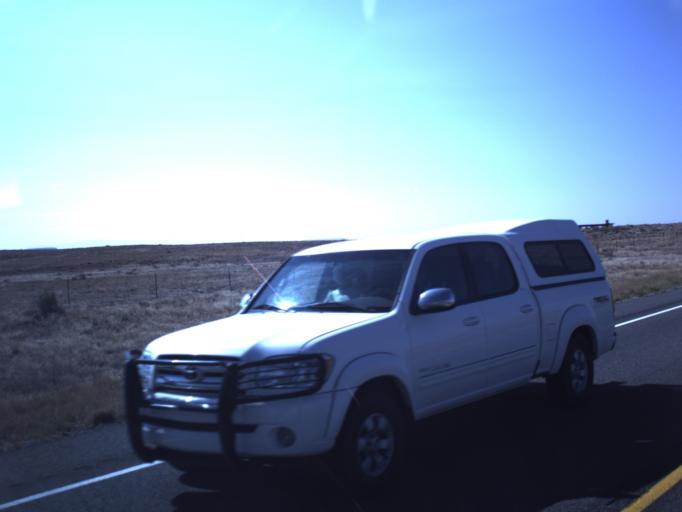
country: US
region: Utah
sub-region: San Juan County
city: Blanding
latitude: 37.4014
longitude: -109.4933
